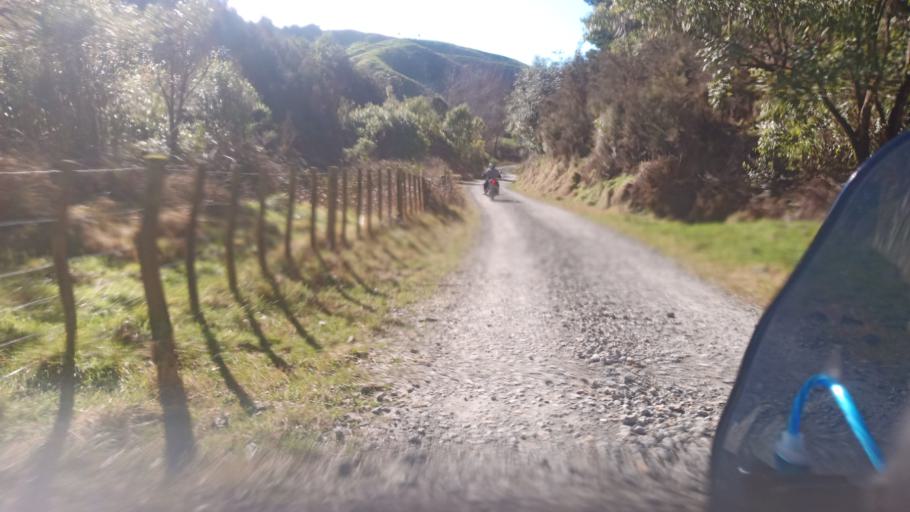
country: NZ
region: Hawke's Bay
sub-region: Wairoa District
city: Wairoa
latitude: -38.6609
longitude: 177.4885
